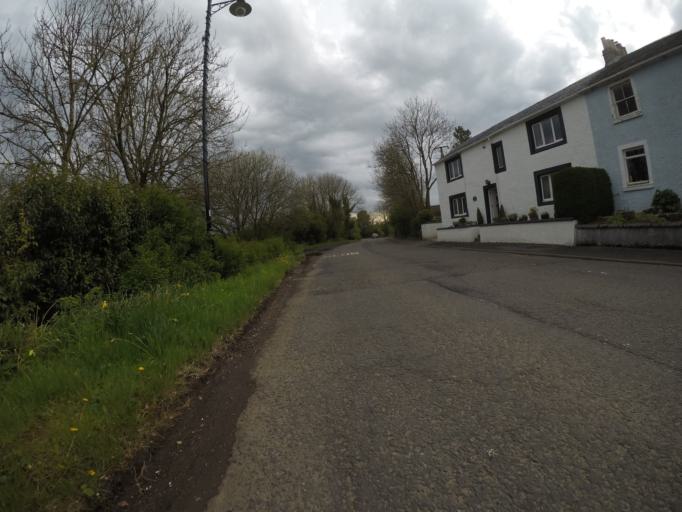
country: GB
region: Scotland
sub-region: East Ayrshire
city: Kilmarnock
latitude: 55.6527
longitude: -4.4479
